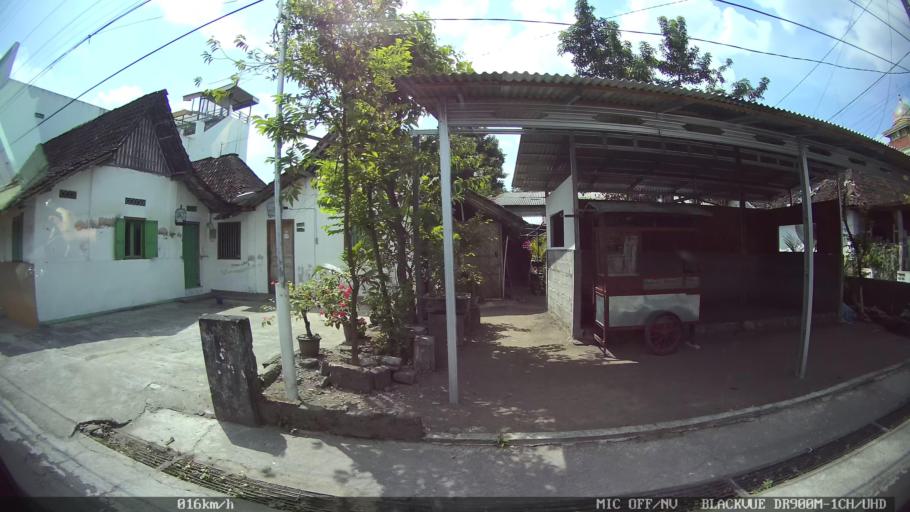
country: ID
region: Daerah Istimewa Yogyakarta
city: Kasihan
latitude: -7.8106
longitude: 110.3401
